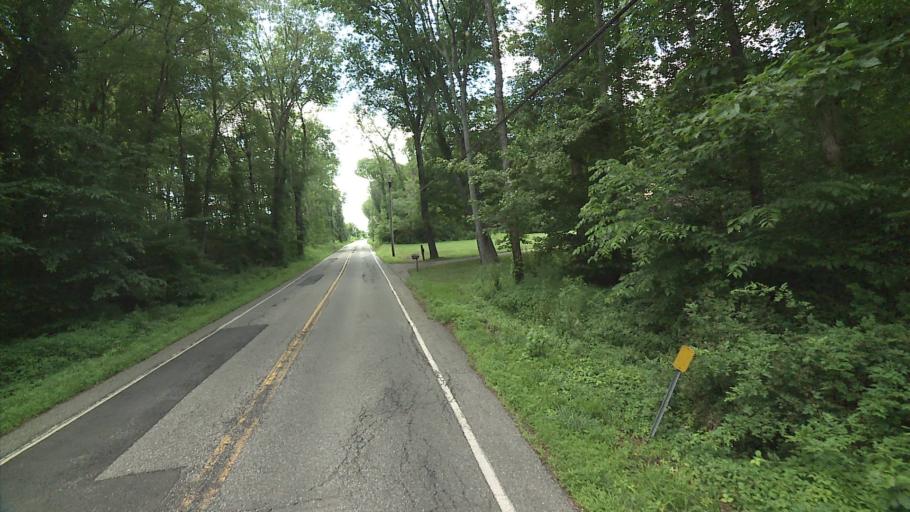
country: US
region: Connecticut
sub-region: New London County
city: Old Mystic
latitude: 41.4355
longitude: -71.9203
